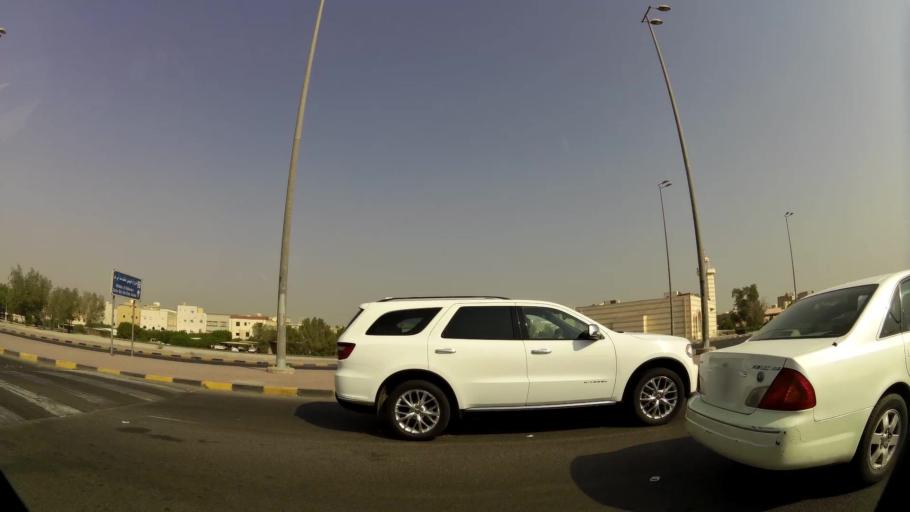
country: KW
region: Al Asimah
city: Ar Rabiyah
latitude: 29.2746
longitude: 47.8694
